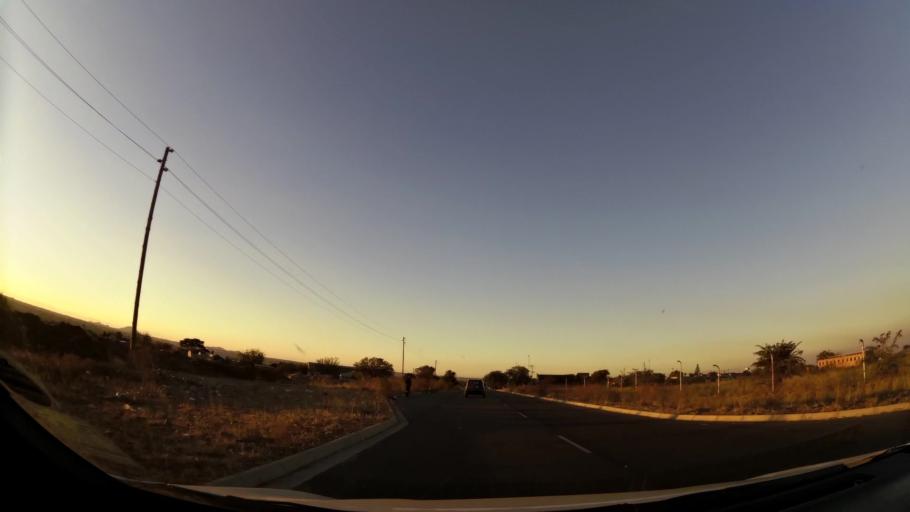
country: ZA
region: Limpopo
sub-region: Capricorn District Municipality
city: Polokwane
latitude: -23.8590
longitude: 29.3751
